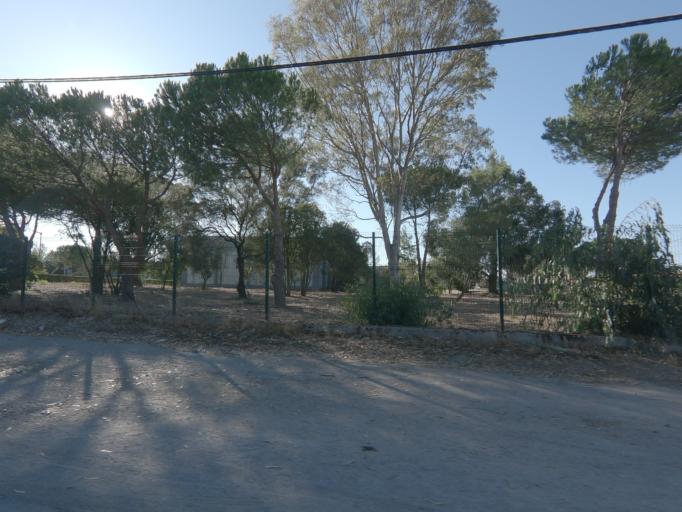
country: PT
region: Setubal
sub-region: Palmela
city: Quinta do Anjo
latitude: 38.5290
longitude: -8.9930
